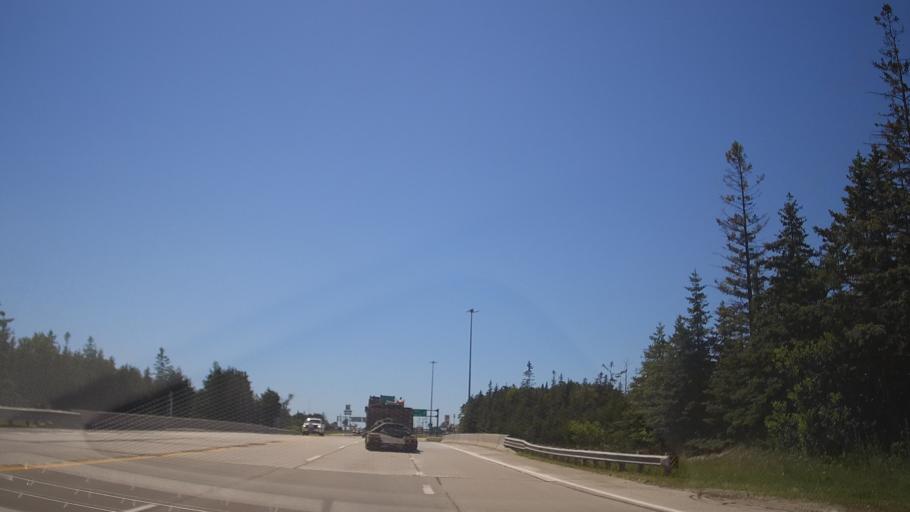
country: US
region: Michigan
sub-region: Mackinac County
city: Saint Ignace
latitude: 45.8577
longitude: -84.7270
